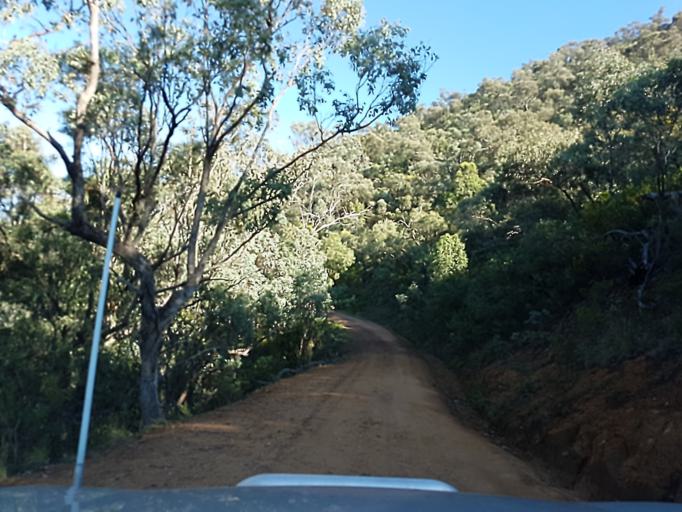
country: AU
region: New South Wales
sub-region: Snowy River
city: Jindabyne
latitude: -36.9333
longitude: 148.3378
